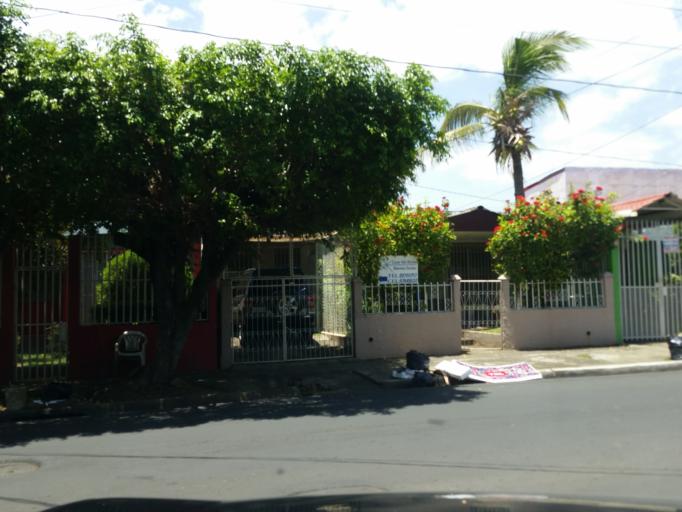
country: NI
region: Managua
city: Managua
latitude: 12.1183
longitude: -86.2515
